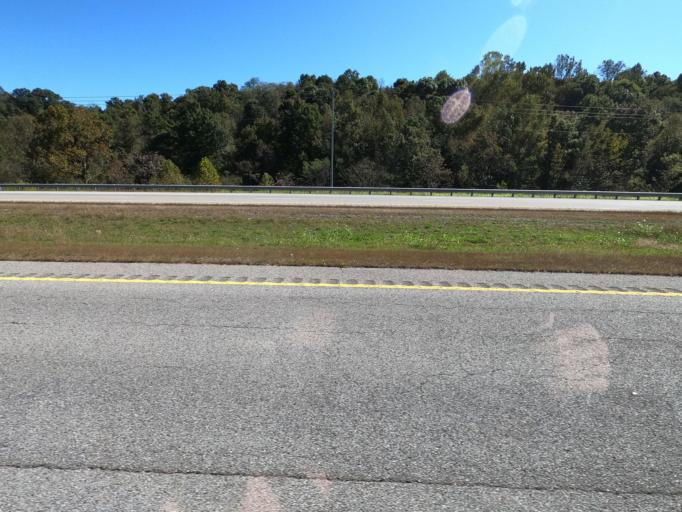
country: US
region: Tennessee
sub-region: Maury County
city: Mount Pleasant
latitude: 35.4774
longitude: -87.2604
